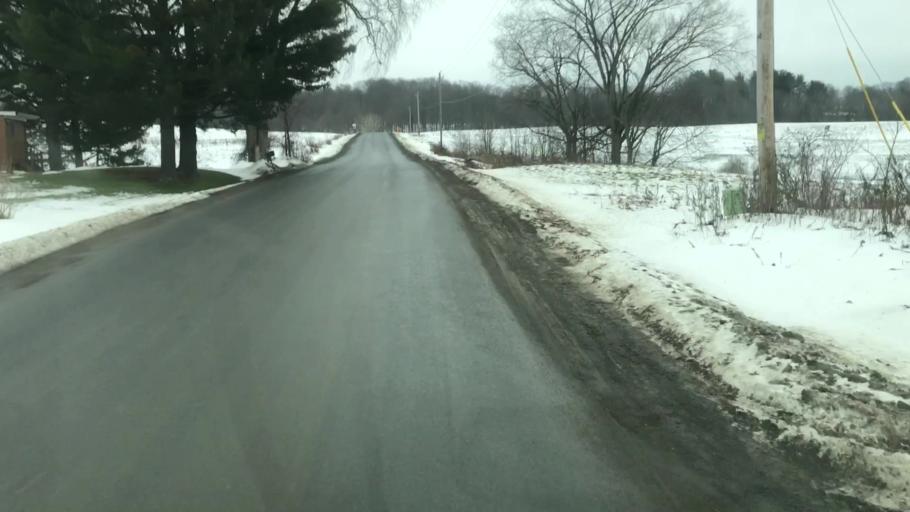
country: US
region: New York
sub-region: Cortland County
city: Cortland West
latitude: 42.6528
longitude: -76.2766
